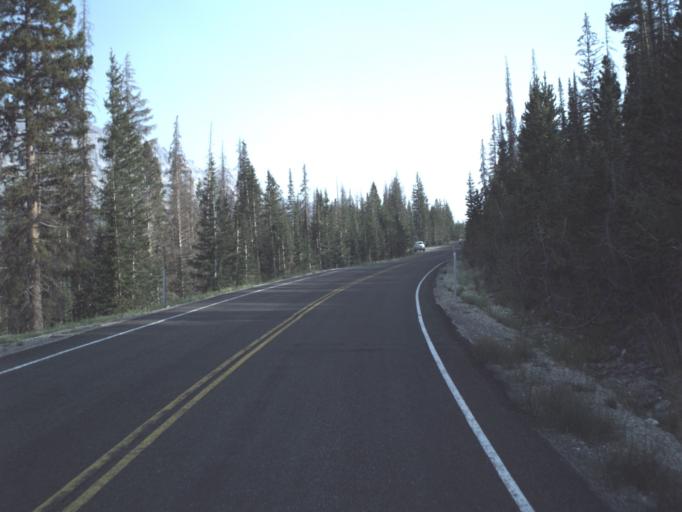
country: US
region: Utah
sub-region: Summit County
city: Kamas
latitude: 40.7547
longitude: -110.8788
